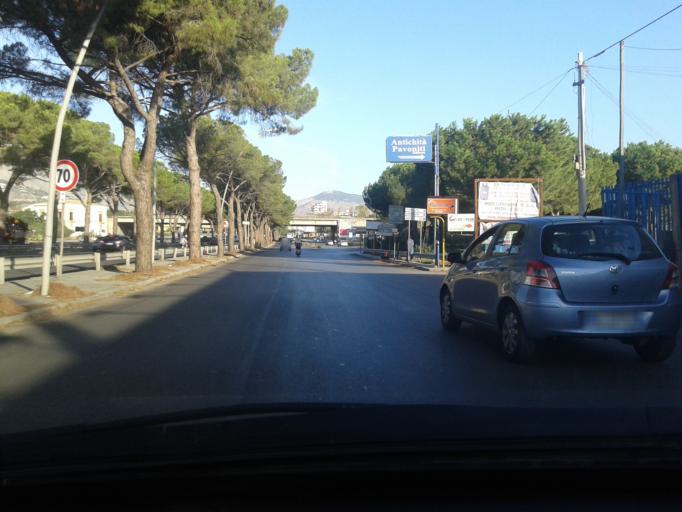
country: IT
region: Sicily
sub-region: Palermo
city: Villa Ciambra
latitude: 38.0925
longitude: 13.3413
